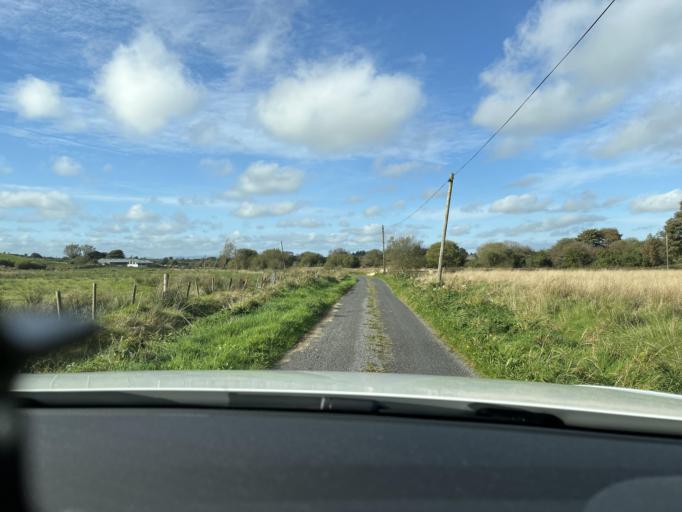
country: IE
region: Connaught
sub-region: Sligo
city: Ballymote
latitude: 54.0706
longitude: -8.4262
